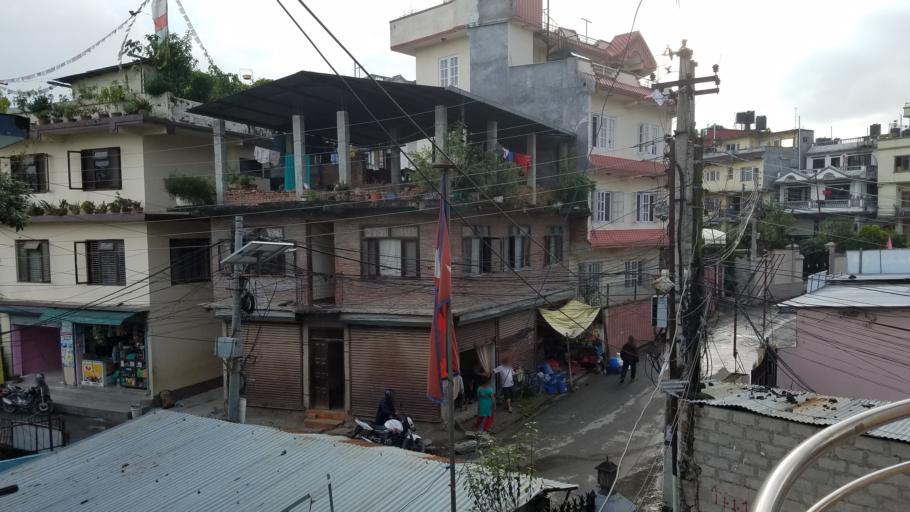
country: NP
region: Central Region
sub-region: Bagmati Zone
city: Kathmandu
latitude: 27.7326
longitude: 85.3386
